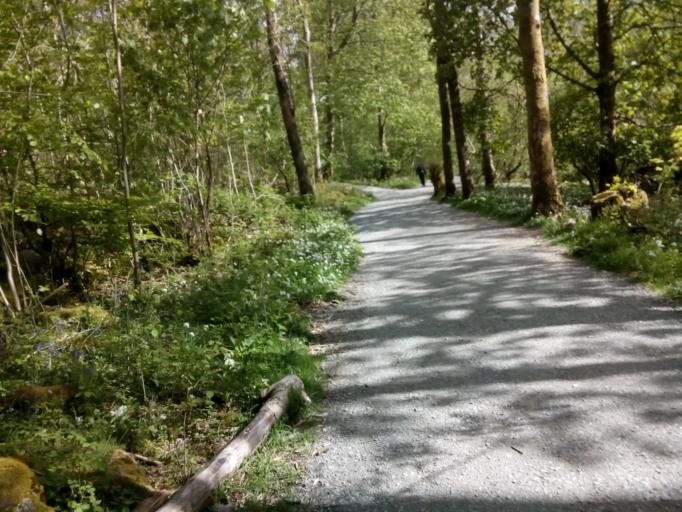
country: GB
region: England
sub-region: Cumbria
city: Ambleside
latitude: 54.4289
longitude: -3.0225
